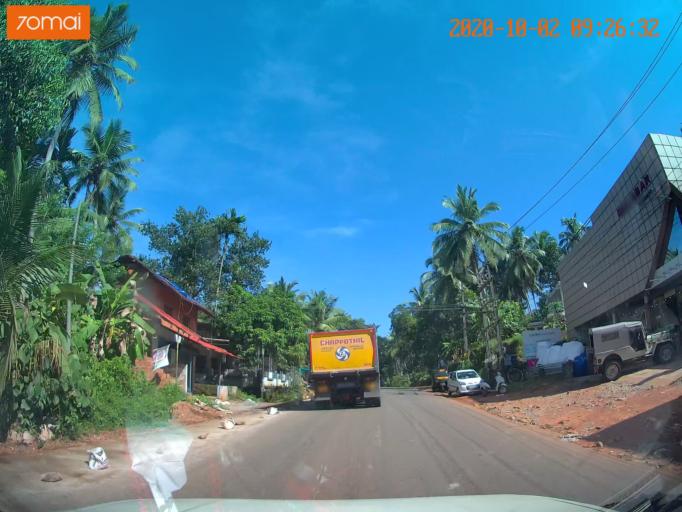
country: IN
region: Kerala
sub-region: Kozhikode
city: Naduvannur
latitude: 11.5930
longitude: 75.7663
